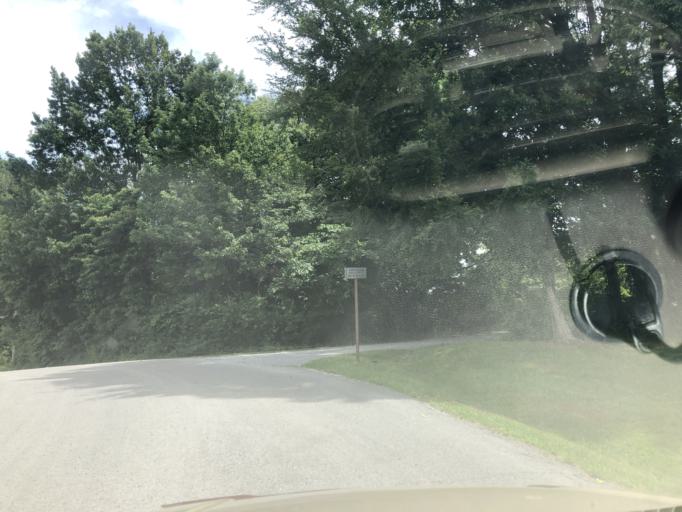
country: US
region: Tennessee
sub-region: Davidson County
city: Lakewood
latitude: 36.2511
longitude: -86.6037
